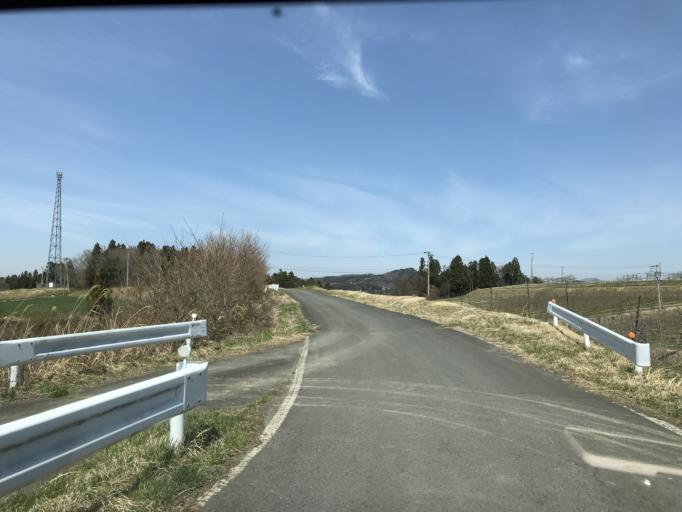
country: JP
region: Iwate
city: Ichinoseki
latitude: 38.8404
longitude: 141.2870
